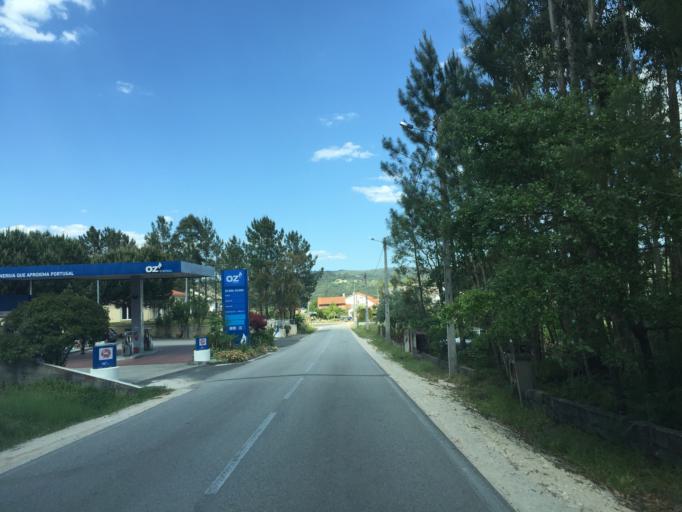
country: PT
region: Leiria
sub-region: Alvaiazere
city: Alvaiazere
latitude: 39.7532
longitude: -8.4657
